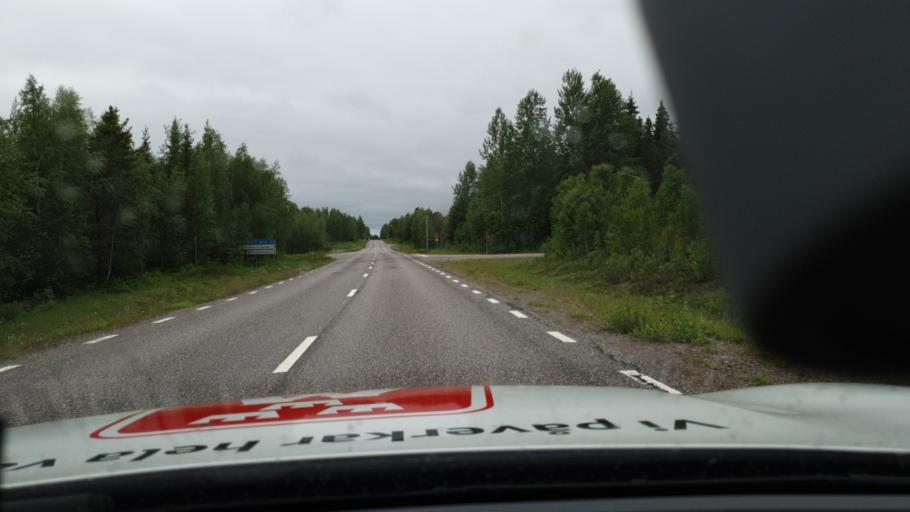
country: SE
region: Norrbotten
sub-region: Pajala Kommun
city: Pajala
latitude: 67.1876
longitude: 23.4806
